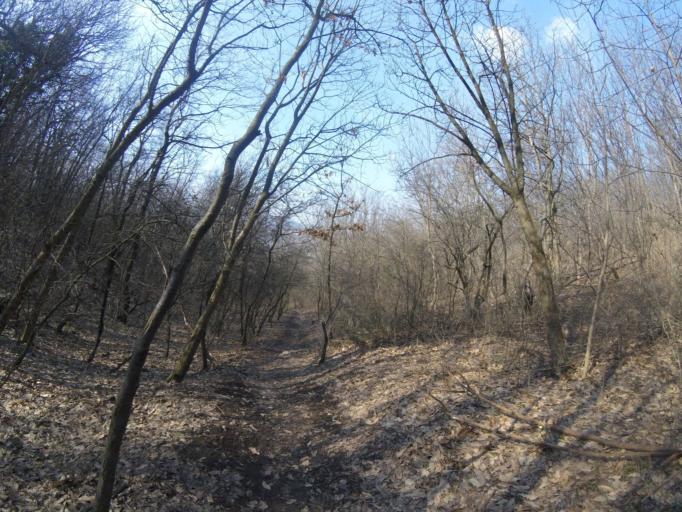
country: HU
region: Komarom-Esztergom
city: Nyergesujfalu
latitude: 47.7297
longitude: 18.5694
